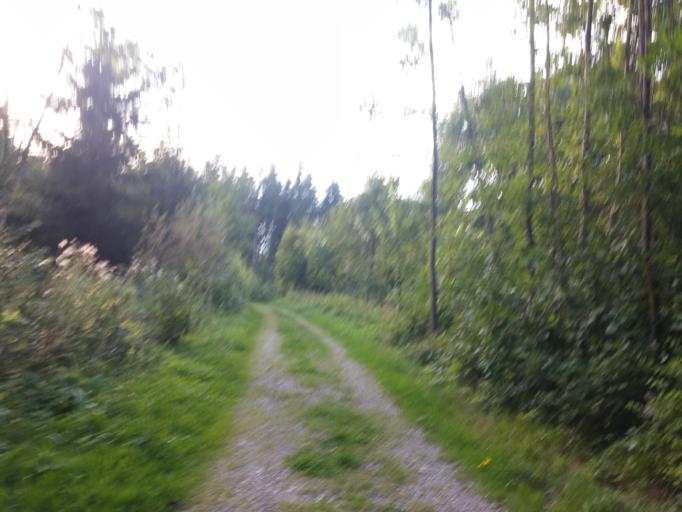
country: DE
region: Bavaria
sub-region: Swabia
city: Buxheim
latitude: 47.9940
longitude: 10.1285
